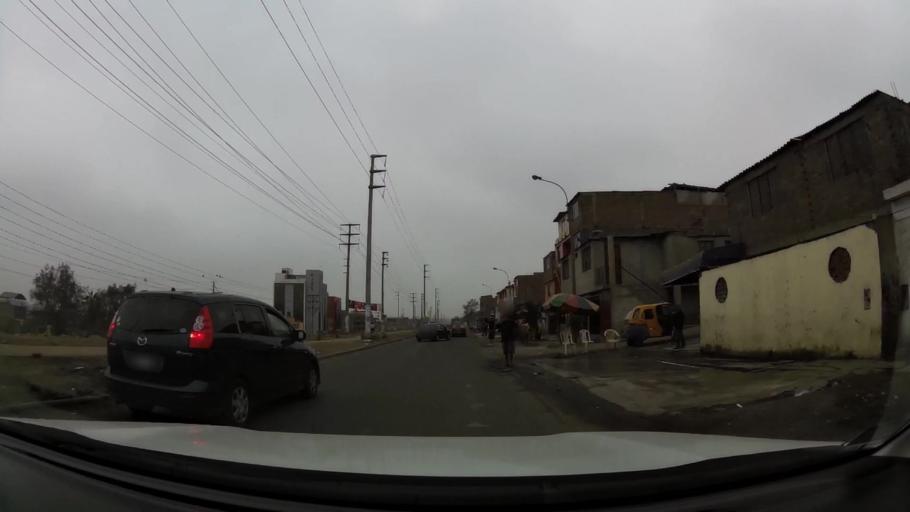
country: PE
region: Lima
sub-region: Lima
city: Surco
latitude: -12.1543
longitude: -76.9623
